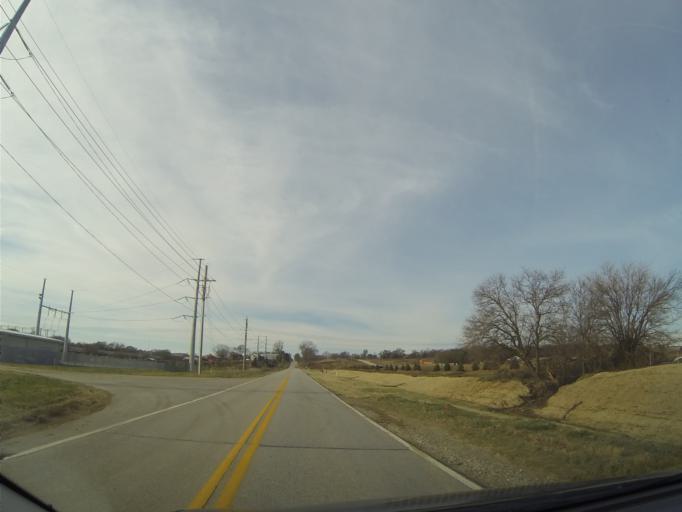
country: US
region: Nebraska
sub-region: Douglas County
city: Elkhorn
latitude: 41.2775
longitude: -96.2038
